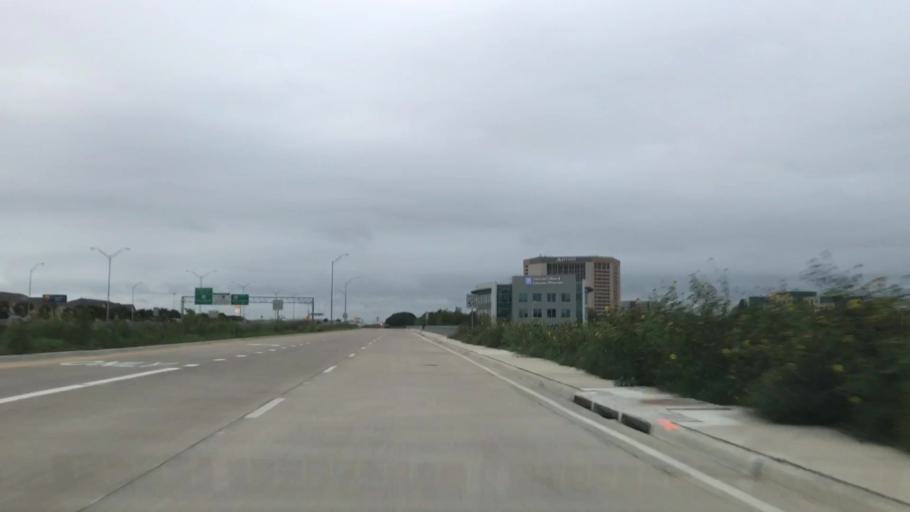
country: US
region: Texas
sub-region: Dallas County
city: Coppell
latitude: 32.9184
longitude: -97.0134
